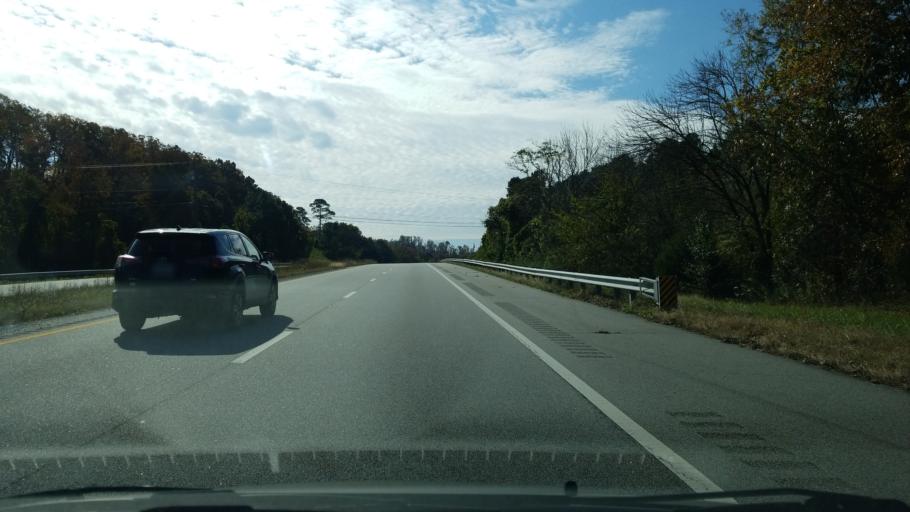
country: US
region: Tennessee
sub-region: Hamilton County
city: Harrison
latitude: 35.1360
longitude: -85.1218
